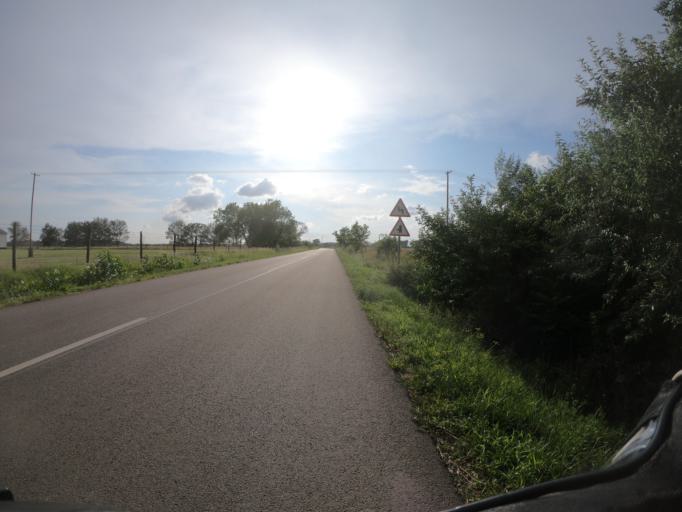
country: HU
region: Borsod-Abauj-Zemplen
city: Mezokeresztes
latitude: 47.8293
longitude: 20.8017
